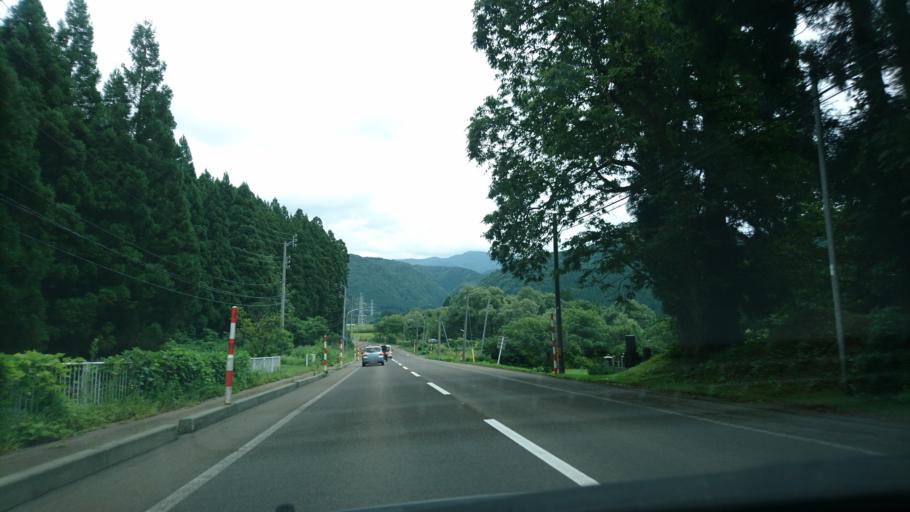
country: JP
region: Akita
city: Yuzawa
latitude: 38.9785
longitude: 140.4982
